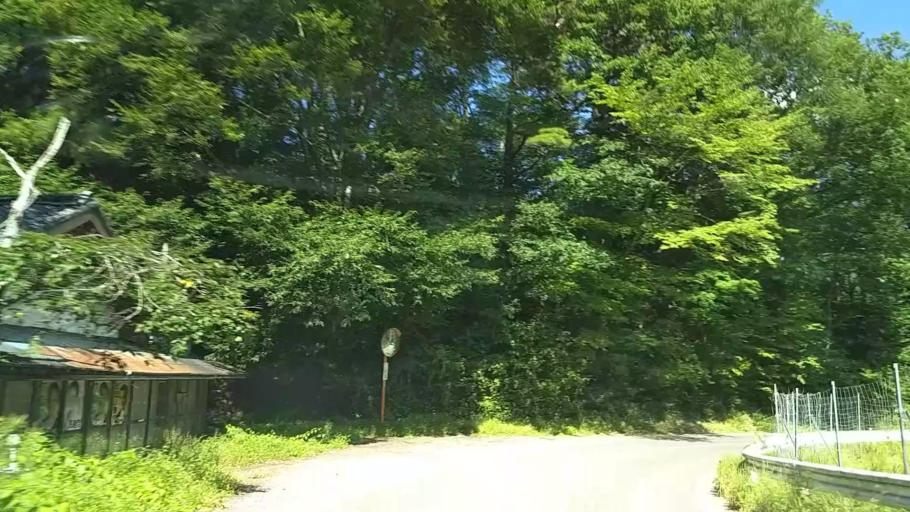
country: JP
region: Nagano
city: Matsumoto
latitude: 36.2097
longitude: 138.0555
